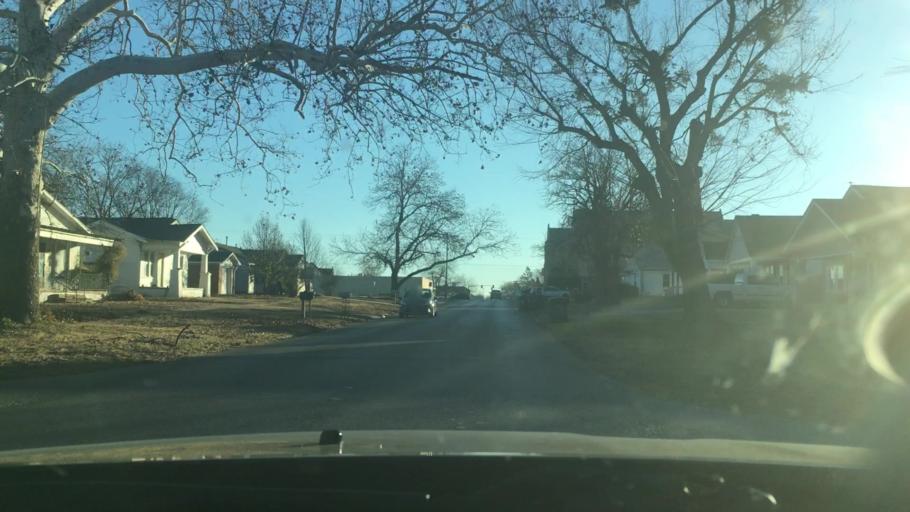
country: US
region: Oklahoma
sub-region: Pontotoc County
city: Ada
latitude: 34.7713
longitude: -96.6819
